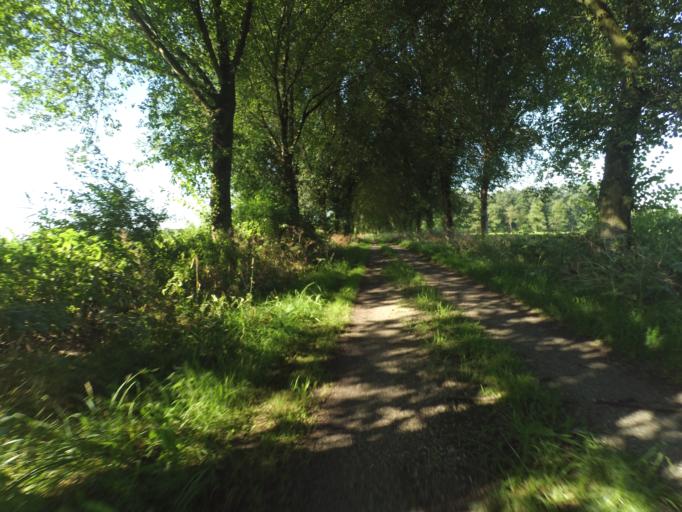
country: NL
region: Flevoland
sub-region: Gemeente Zeewolde
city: Zeewolde
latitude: 52.3989
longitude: 5.4960
